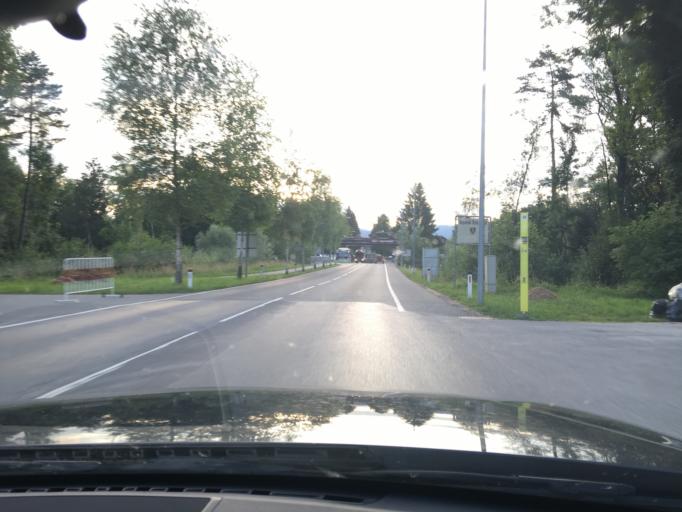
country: AT
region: Vorarlberg
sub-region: Politischer Bezirk Dornbirn
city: Hohenems
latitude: 47.3773
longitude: 9.6716
